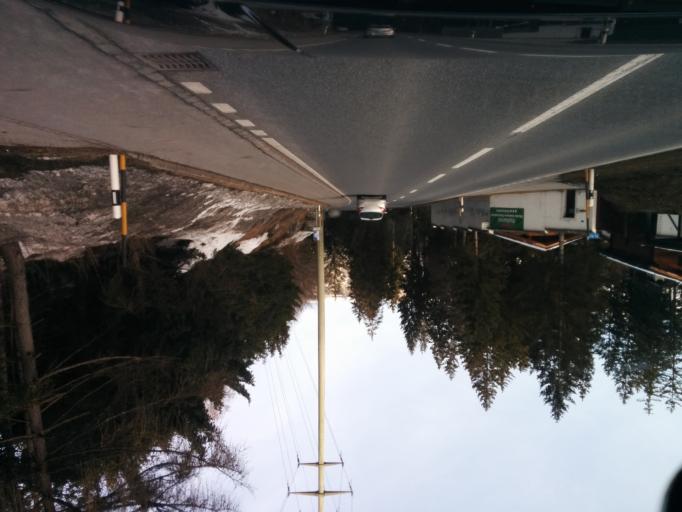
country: CH
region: Grisons
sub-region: Surselva District
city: Laax
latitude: 46.8195
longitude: 9.2679
